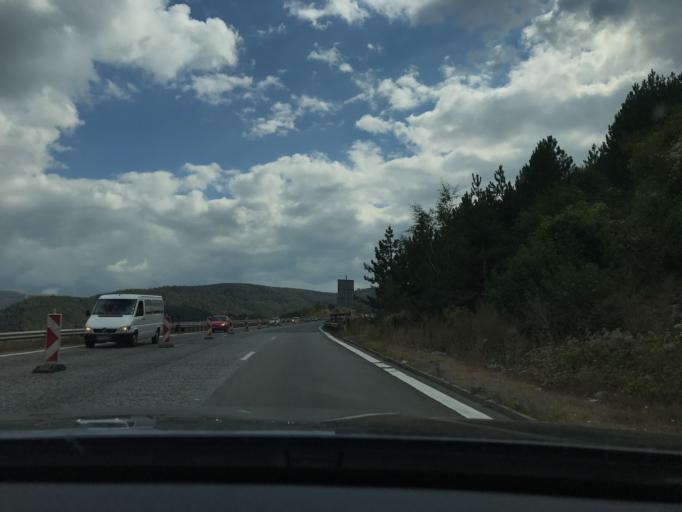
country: BG
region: Sofiya
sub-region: Obshtina Botevgrad
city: Botevgrad
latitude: 42.8052
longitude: 23.8085
